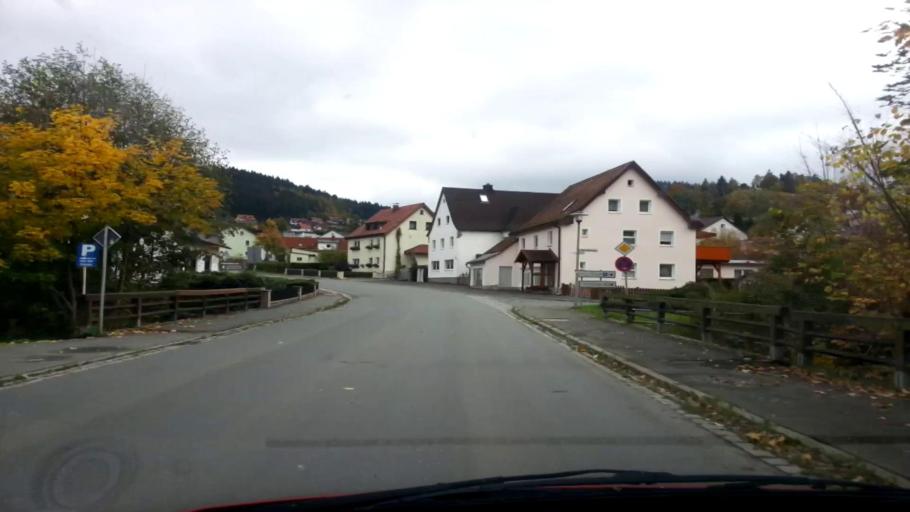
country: DE
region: Bavaria
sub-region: Upper Franconia
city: Warmensteinach
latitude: 49.9989
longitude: 11.7813
